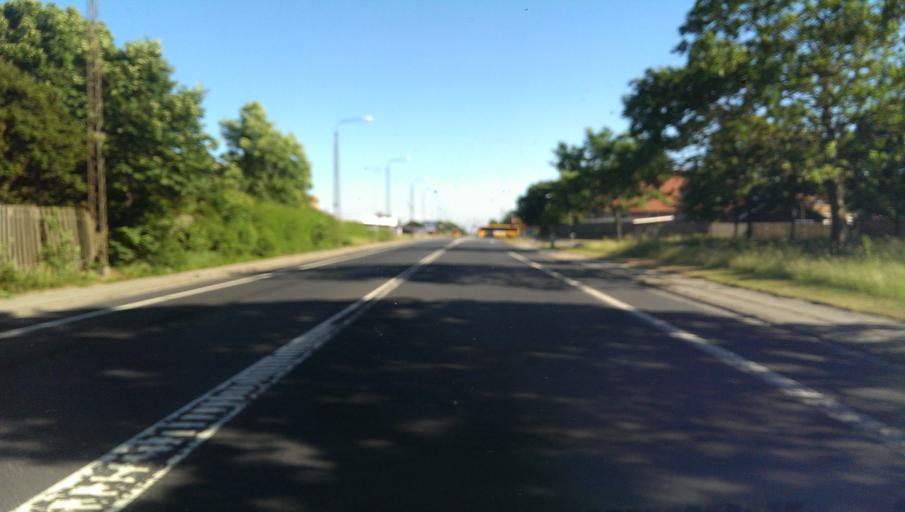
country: DK
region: South Denmark
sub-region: Esbjerg Kommune
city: Esbjerg
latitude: 55.5012
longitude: 8.4064
